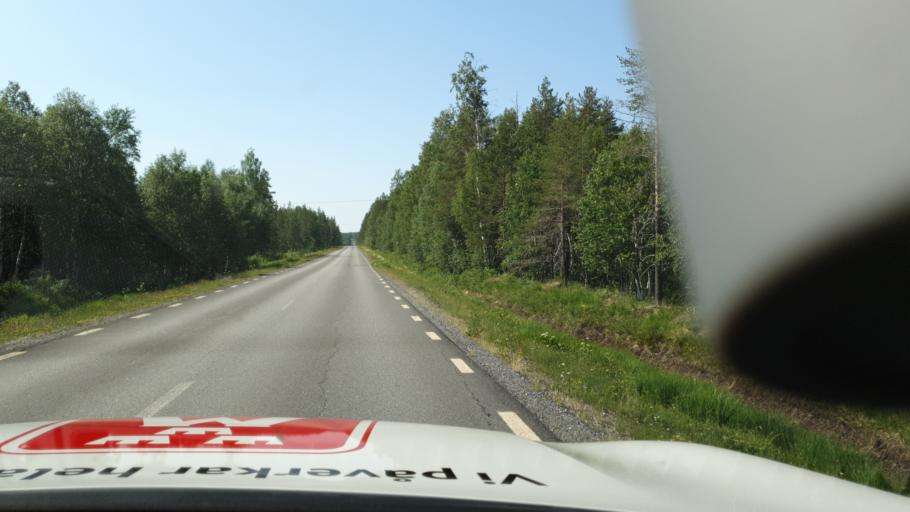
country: SE
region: Vaesterbotten
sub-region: Skelleftea Kommun
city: Langsele
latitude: 64.9873
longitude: 20.0799
